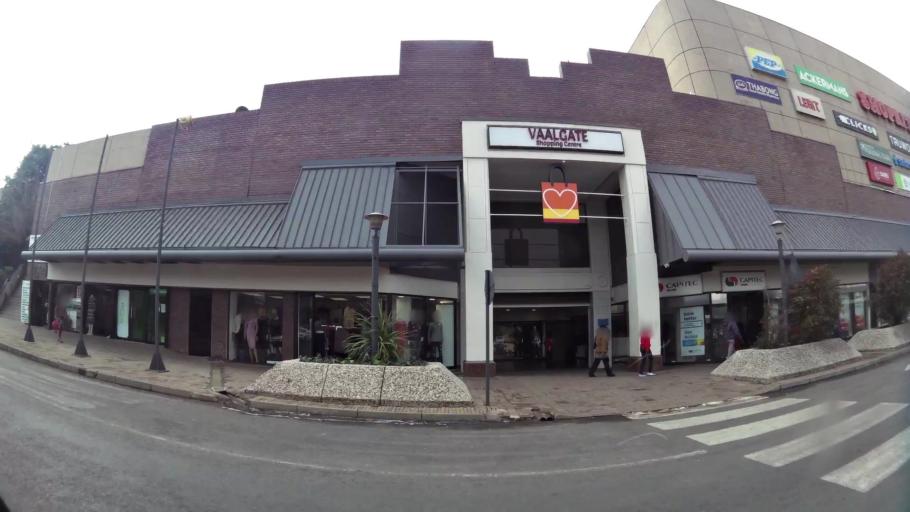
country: ZA
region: Gauteng
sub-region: Sedibeng District Municipality
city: Vanderbijlpark
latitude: -26.6985
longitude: 27.8376
